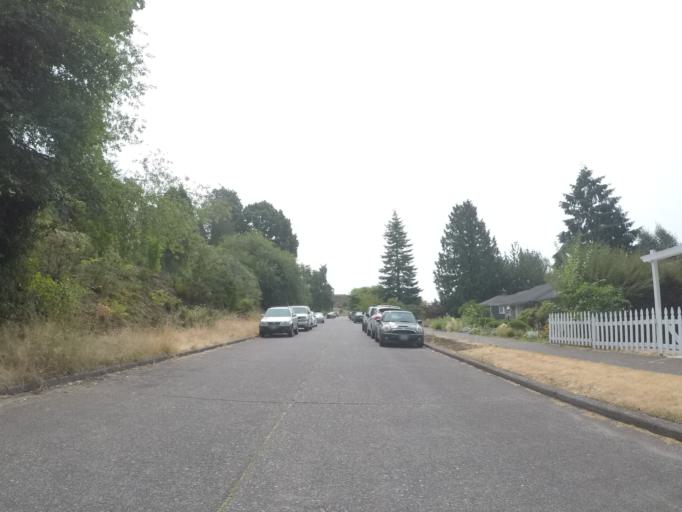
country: US
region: Washington
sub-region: King County
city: Seattle
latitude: 47.5756
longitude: -122.3908
